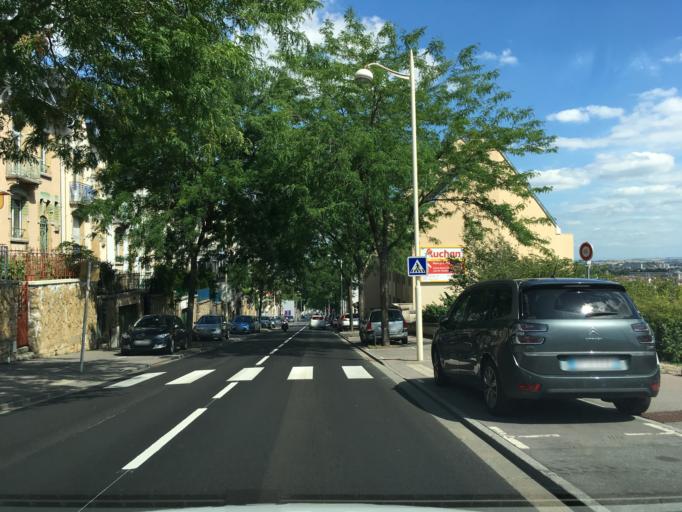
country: FR
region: Lorraine
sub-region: Departement de Meurthe-et-Moselle
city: Laxou
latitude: 48.6908
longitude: 6.1543
